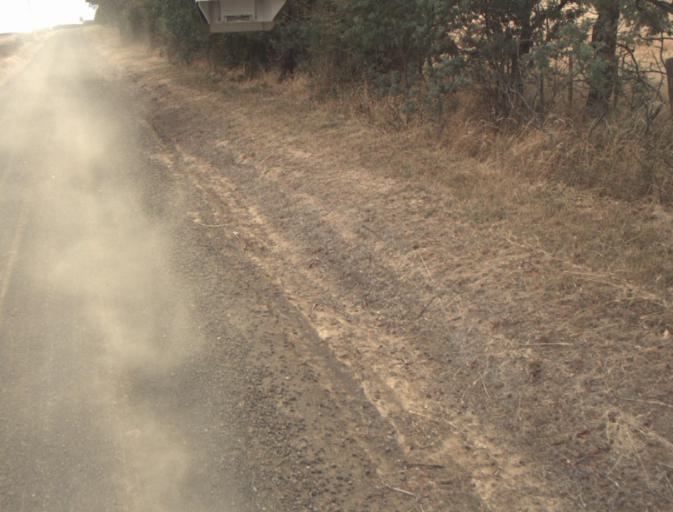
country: AU
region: Tasmania
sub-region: Northern Midlands
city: Evandale
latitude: -41.5159
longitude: 147.2934
